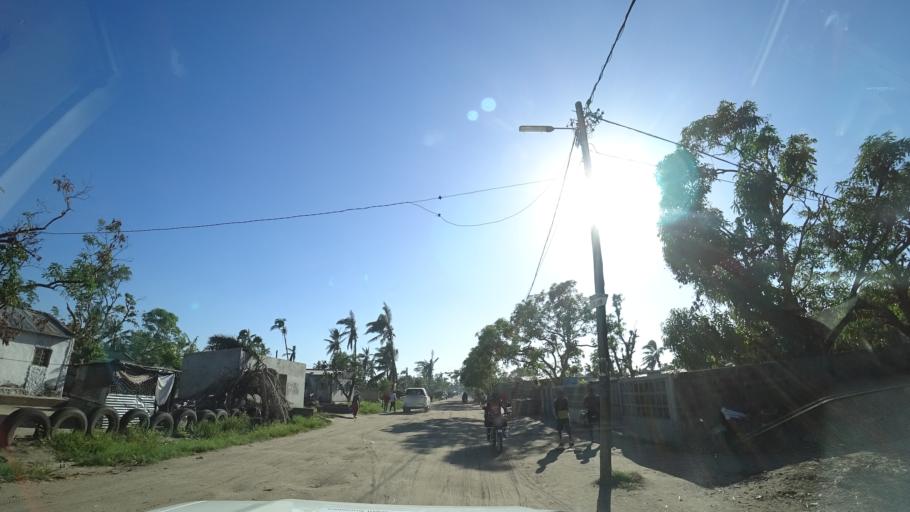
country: MZ
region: Sofala
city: Beira
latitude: -19.7736
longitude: 34.8852
